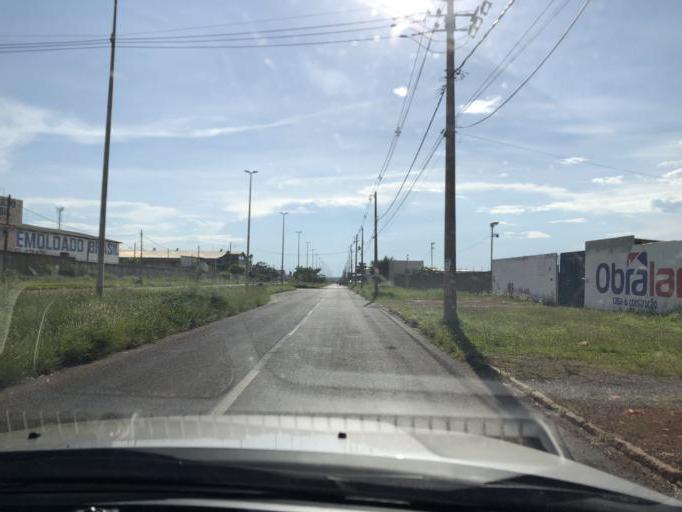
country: BR
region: Federal District
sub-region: Brasilia
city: Brasilia
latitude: -15.7910
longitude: -48.1449
